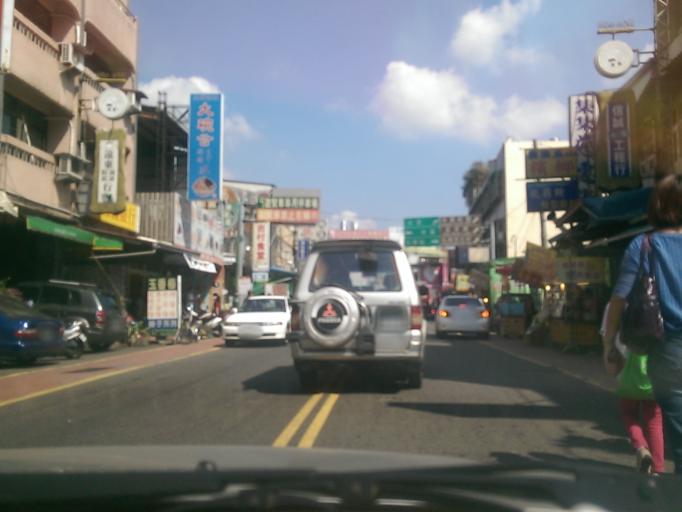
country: TW
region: Taiwan
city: Lugu
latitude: 23.8269
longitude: 120.7840
